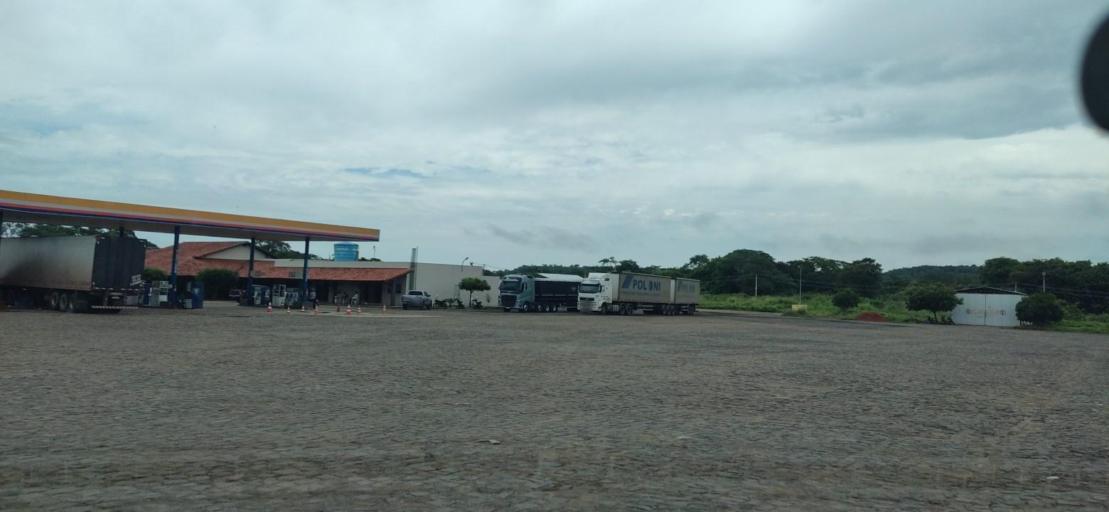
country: BR
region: Piaui
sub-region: Elesbao Veloso
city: Elesbao Veloso
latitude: -6.1887
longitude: -42.1203
